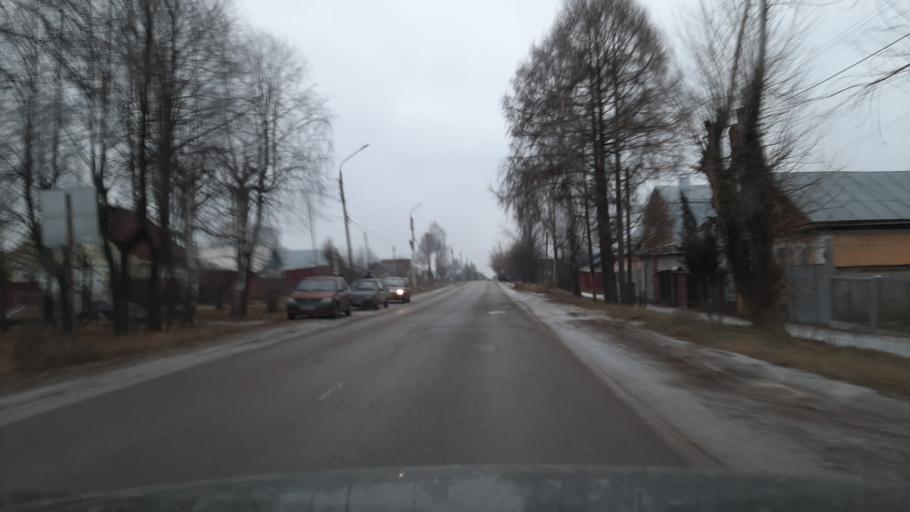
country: RU
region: Ivanovo
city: Shuya
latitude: 56.8721
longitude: 41.3540
